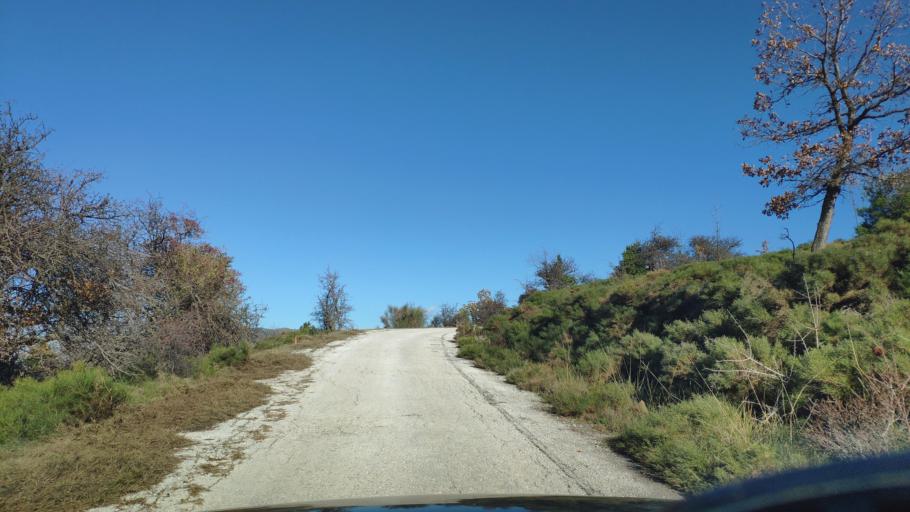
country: GR
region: West Greece
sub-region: Nomos Achaias
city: Aiyira
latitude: 38.0418
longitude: 22.4551
